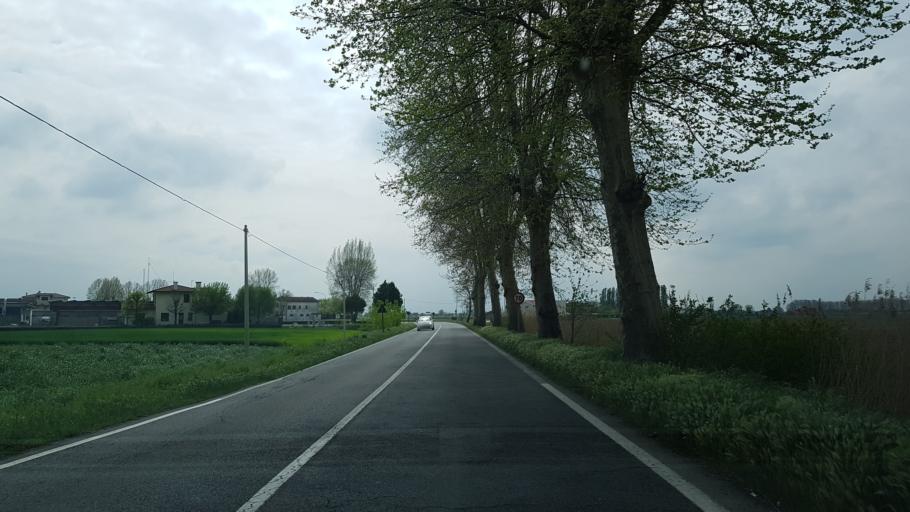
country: IT
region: Veneto
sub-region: Provincia di Verona
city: Minerbe
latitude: 45.2353
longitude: 11.3320
